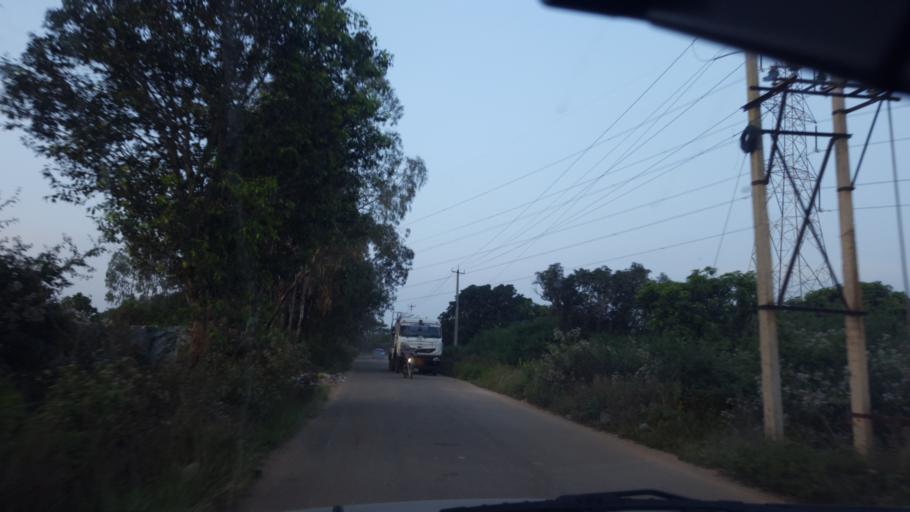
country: IN
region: Karnataka
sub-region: Bangalore Urban
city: Yelahanka
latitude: 13.0711
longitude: 77.6897
